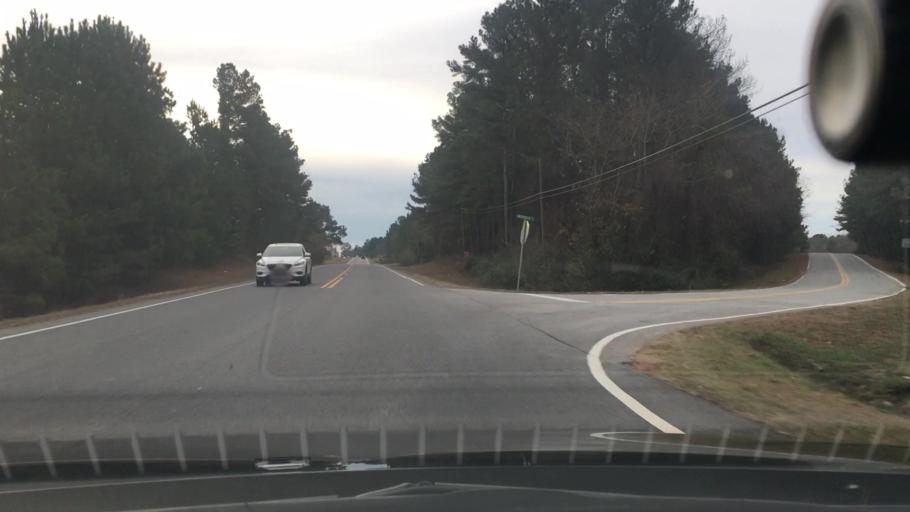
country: US
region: Georgia
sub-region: Coweta County
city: Senoia
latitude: 33.2828
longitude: -84.5369
